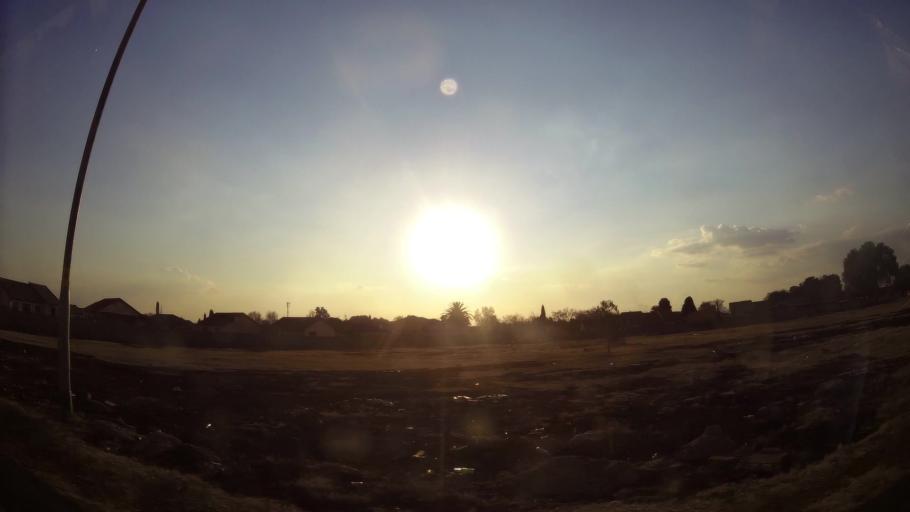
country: ZA
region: Gauteng
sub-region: Ekurhuleni Metropolitan Municipality
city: Boksburg
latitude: -26.2979
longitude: 28.2491
